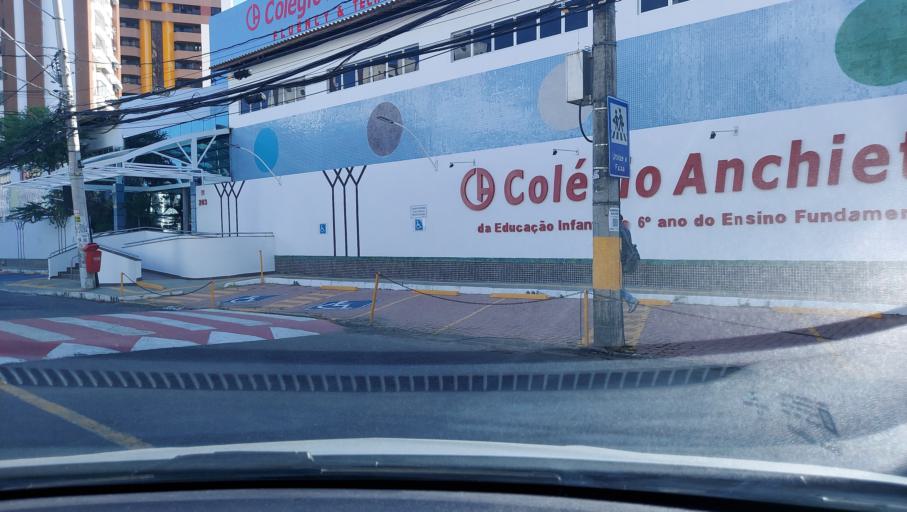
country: BR
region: Bahia
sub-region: Salvador
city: Salvador
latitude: -12.9890
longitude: -38.4530
